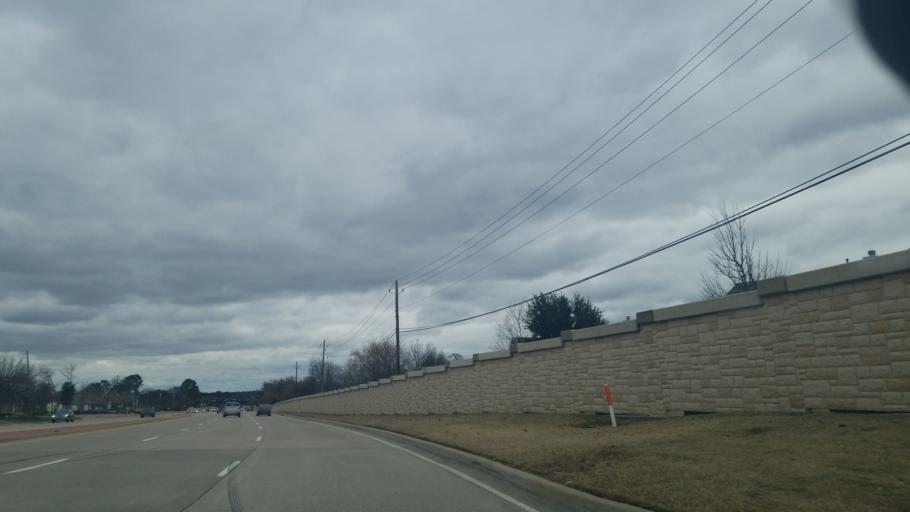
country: US
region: Texas
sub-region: Denton County
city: Flower Mound
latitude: 33.0380
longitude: -97.0694
